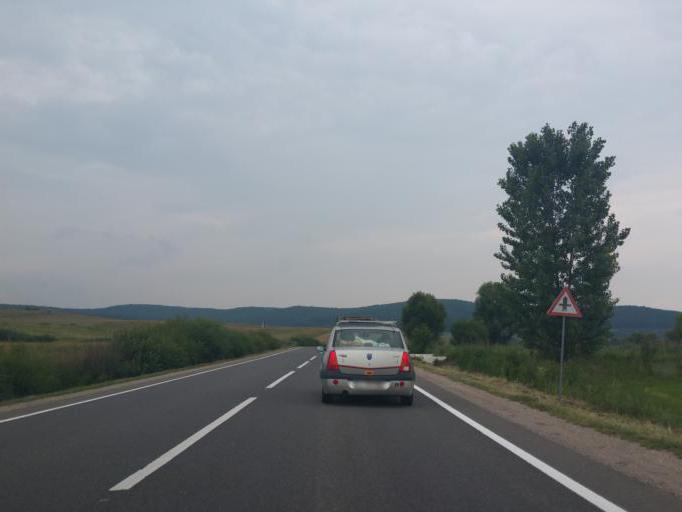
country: RO
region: Cluj
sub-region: Comuna Sanpaul
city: Sanpaul
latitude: 46.8833
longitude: 23.4185
